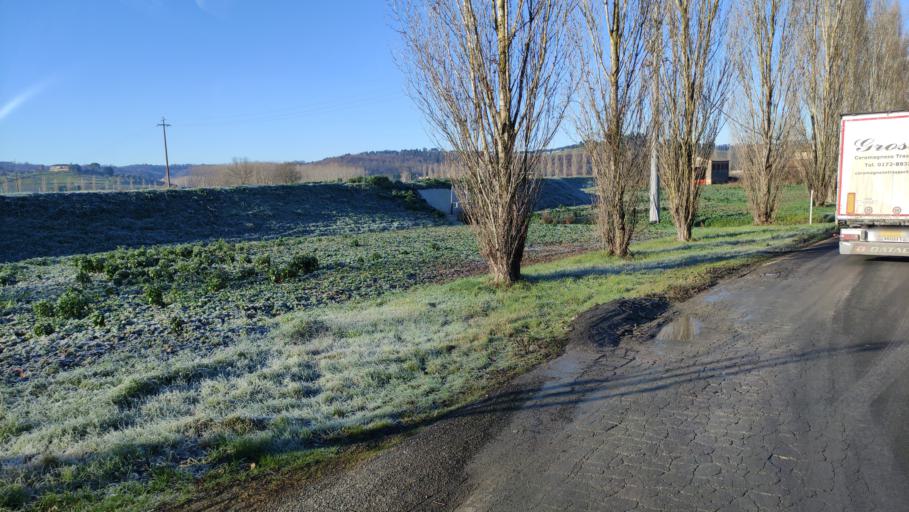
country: IT
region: Tuscany
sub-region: Province of Florence
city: Castelfiorentino
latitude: 43.6466
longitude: 10.9464
